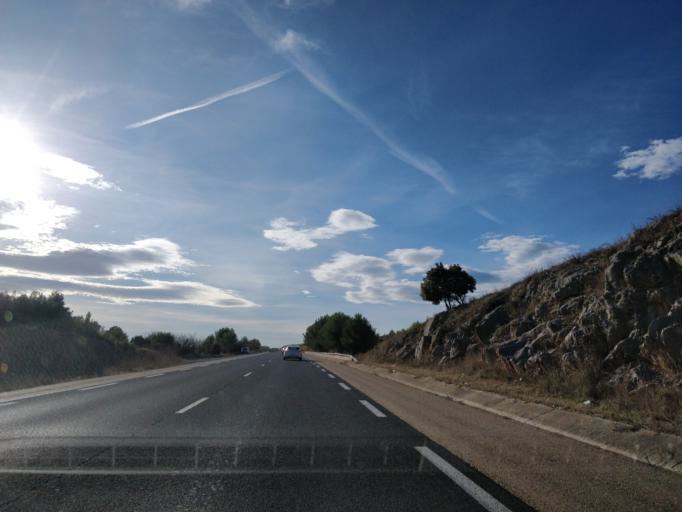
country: FR
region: Languedoc-Roussillon
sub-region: Departement de l'Herault
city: Teyran
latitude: 43.6949
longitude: 3.9431
